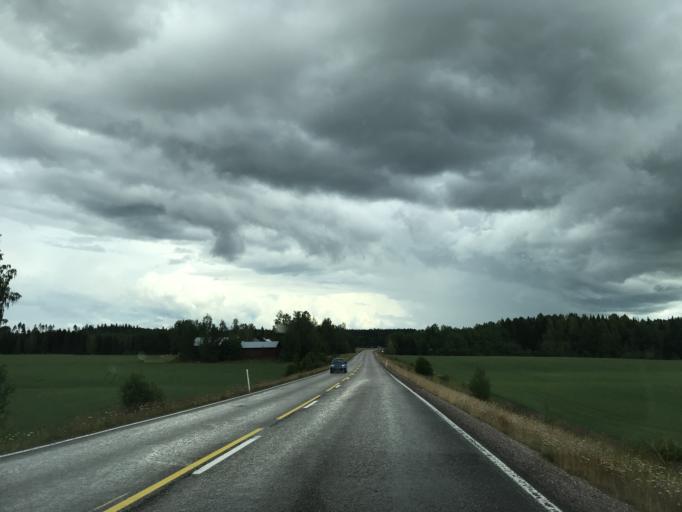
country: FI
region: Uusimaa
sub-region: Porvoo
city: Pukkila
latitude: 60.7727
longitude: 25.5516
